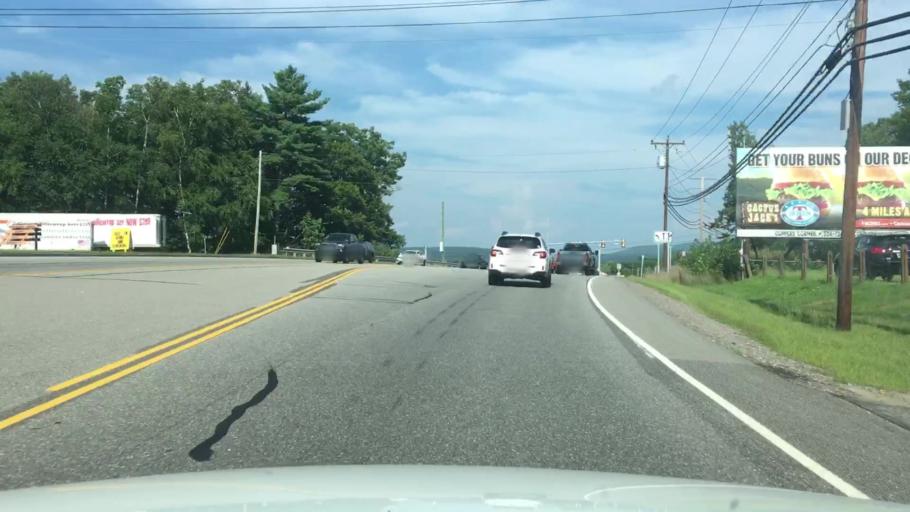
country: US
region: New Hampshire
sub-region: Belknap County
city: Laconia
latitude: 43.5132
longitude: -71.4947
